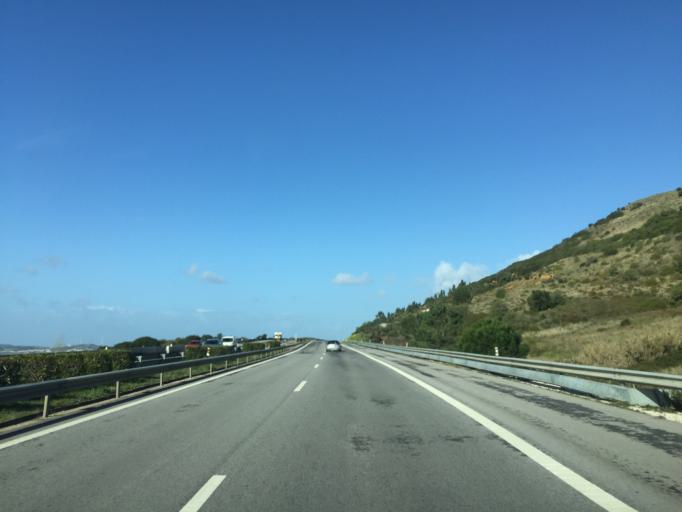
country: PT
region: Lisbon
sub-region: Torres Vedras
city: Torres Vedras
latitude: 39.0340
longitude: -9.2288
